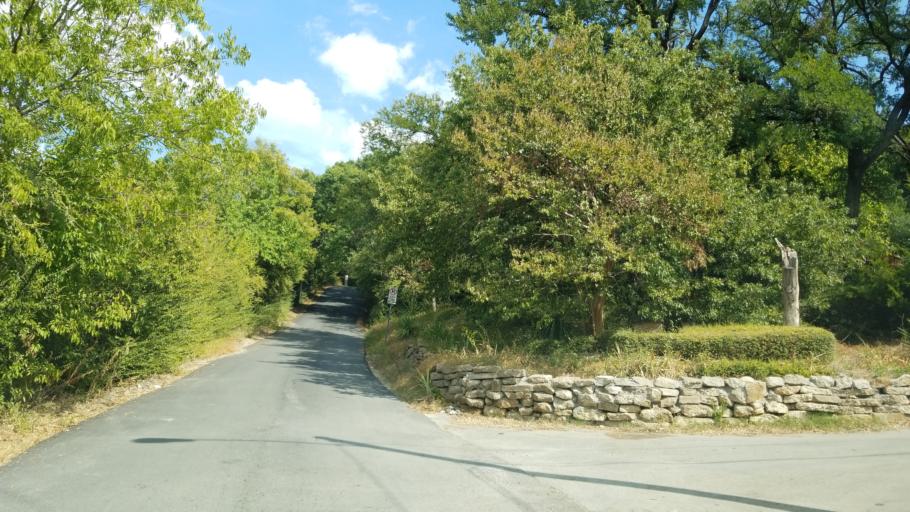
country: US
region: Texas
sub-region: Dallas County
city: Dallas
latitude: 32.7714
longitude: -96.8454
